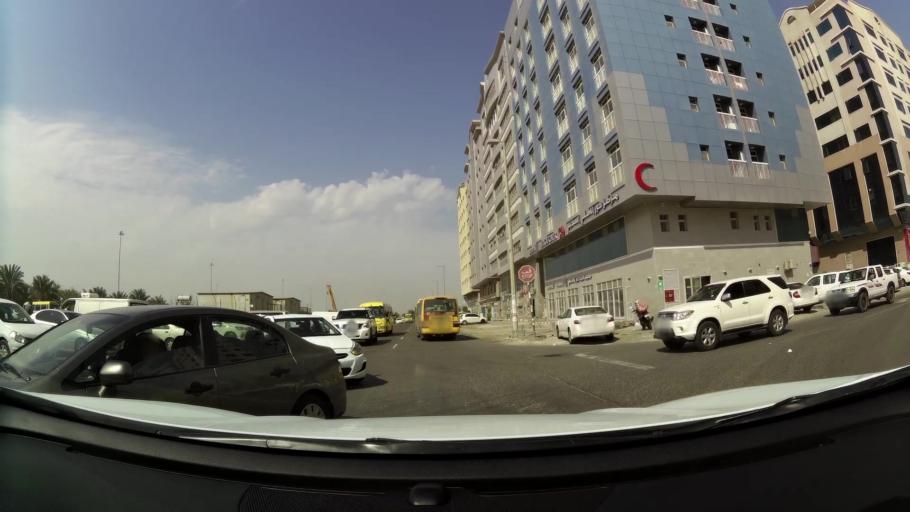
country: AE
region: Abu Dhabi
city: Abu Dhabi
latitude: 24.3432
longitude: 54.5299
